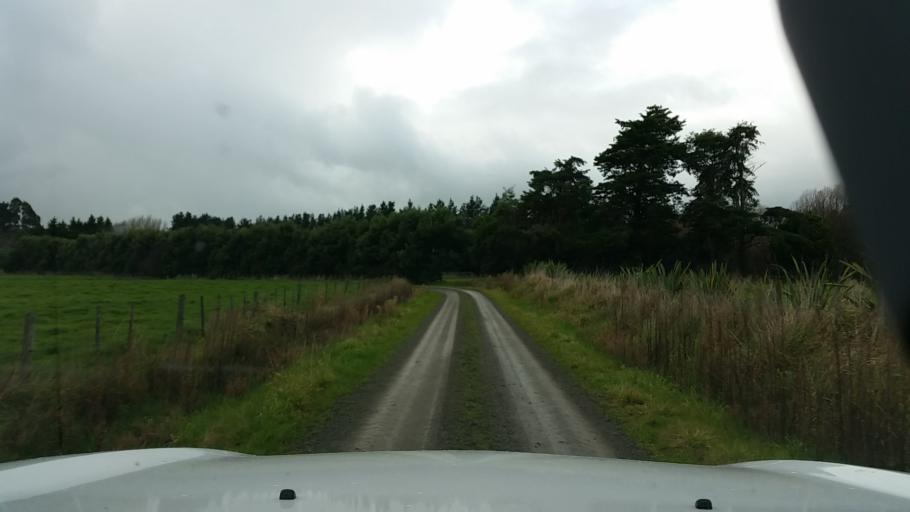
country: NZ
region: Wellington
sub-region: Masterton District
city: Masterton
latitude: -41.0928
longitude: 175.5169
